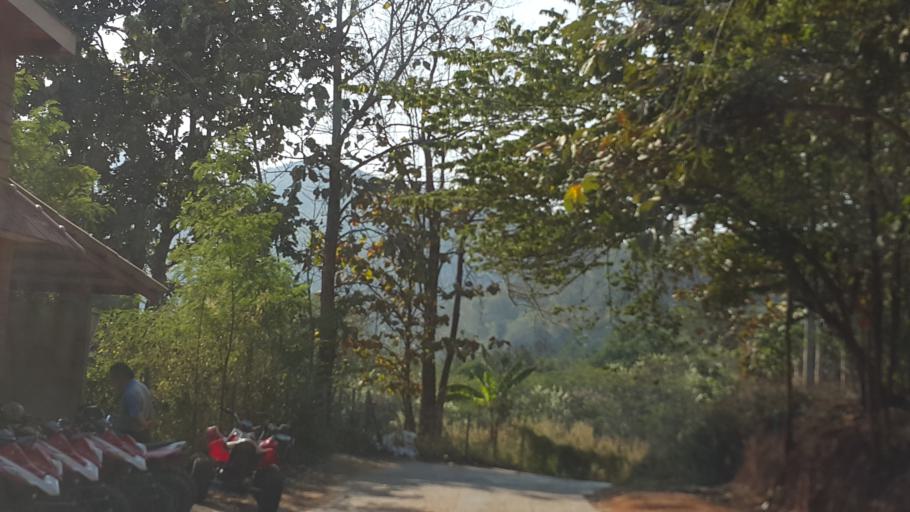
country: TH
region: Chiang Mai
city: Mae Taeng
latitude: 19.2209
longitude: 98.8505
